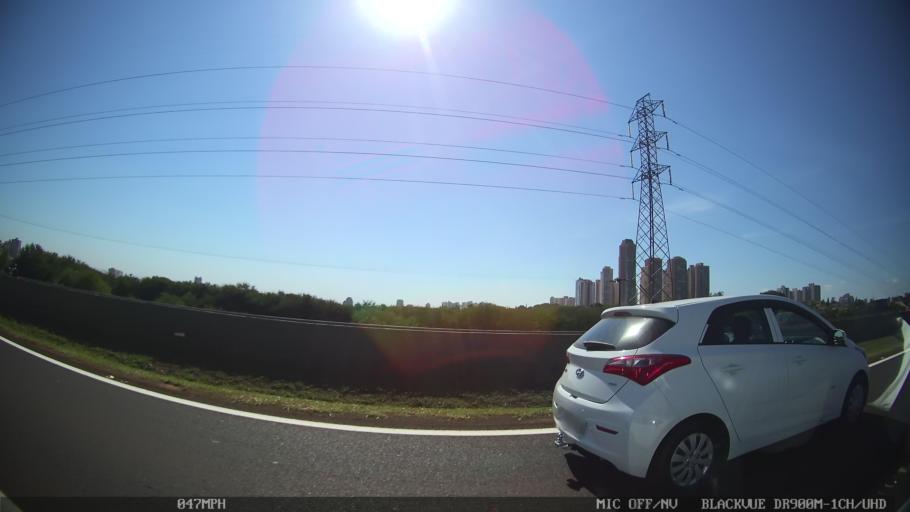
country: BR
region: Sao Paulo
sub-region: Ribeirao Preto
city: Ribeirao Preto
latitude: -21.2249
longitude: -47.8075
